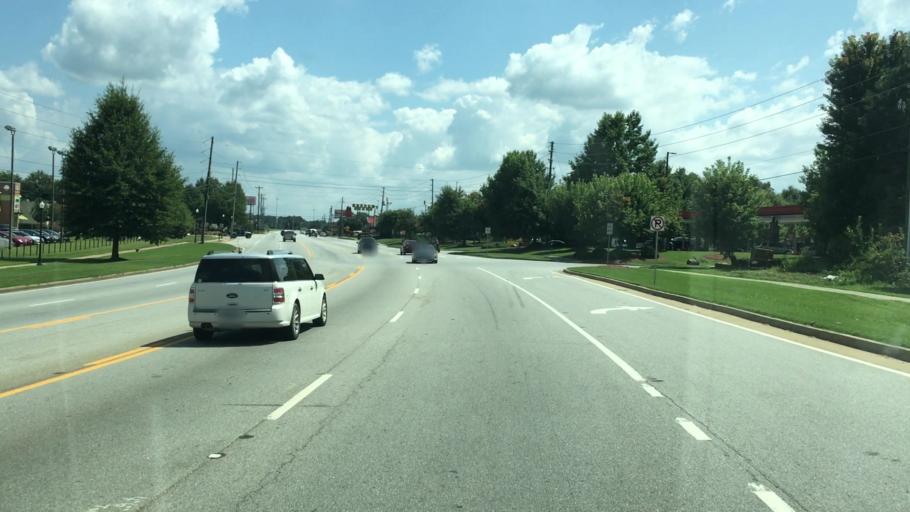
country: US
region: Georgia
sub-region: Morgan County
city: Madison
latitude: 33.5620
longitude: -83.4784
